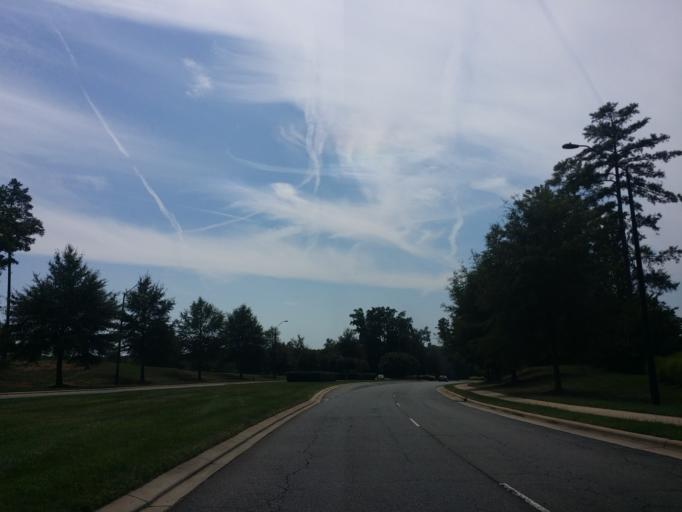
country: US
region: North Carolina
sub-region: Wake County
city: Morrisville
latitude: 35.9052
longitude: -78.7864
